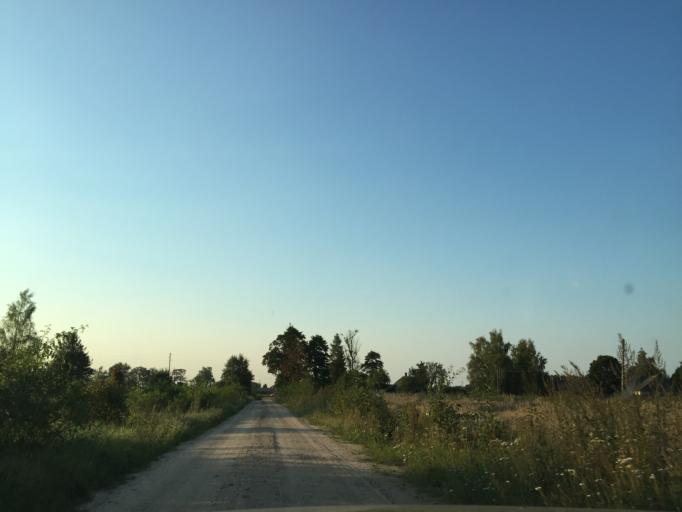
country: LV
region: Limbazu Rajons
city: Limbazi
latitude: 57.5698
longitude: 24.7706
